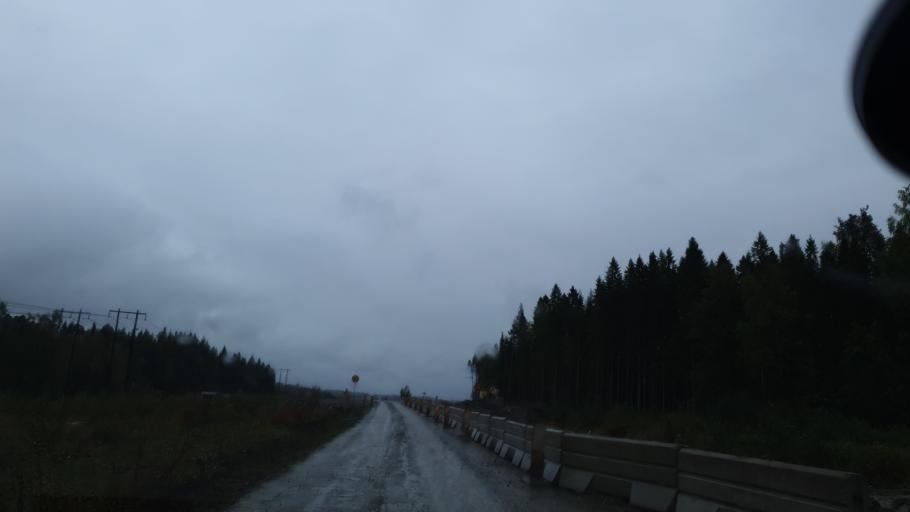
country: SE
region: Vaesterbotten
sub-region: Skelleftea Kommun
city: Soedra Bergsbyn
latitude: 64.7417
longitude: 21.0713
